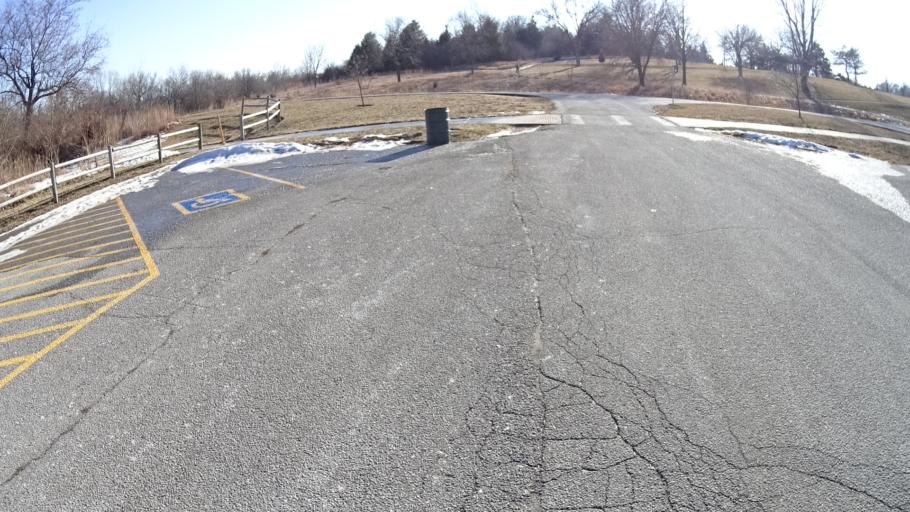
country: US
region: Nebraska
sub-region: Douglas County
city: Bennington
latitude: 41.3127
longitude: -96.1318
